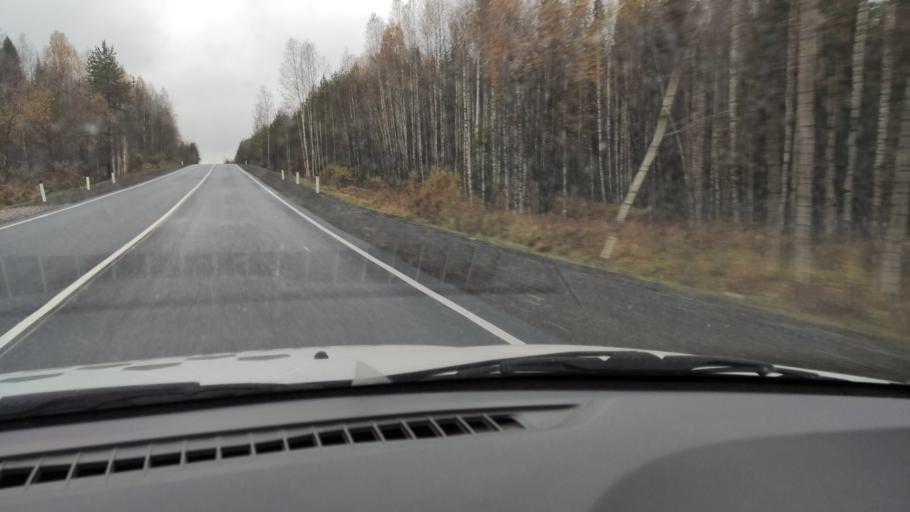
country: RU
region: Kirov
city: Chernaya Kholunitsa
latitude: 58.8730
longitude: 51.5141
